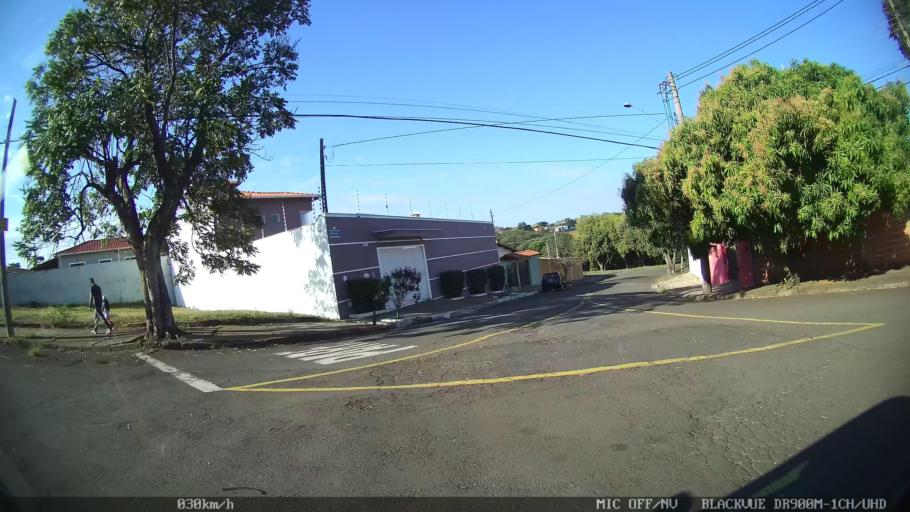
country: BR
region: Sao Paulo
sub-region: Piracicaba
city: Piracicaba
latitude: -22.6848
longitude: -47.6351
